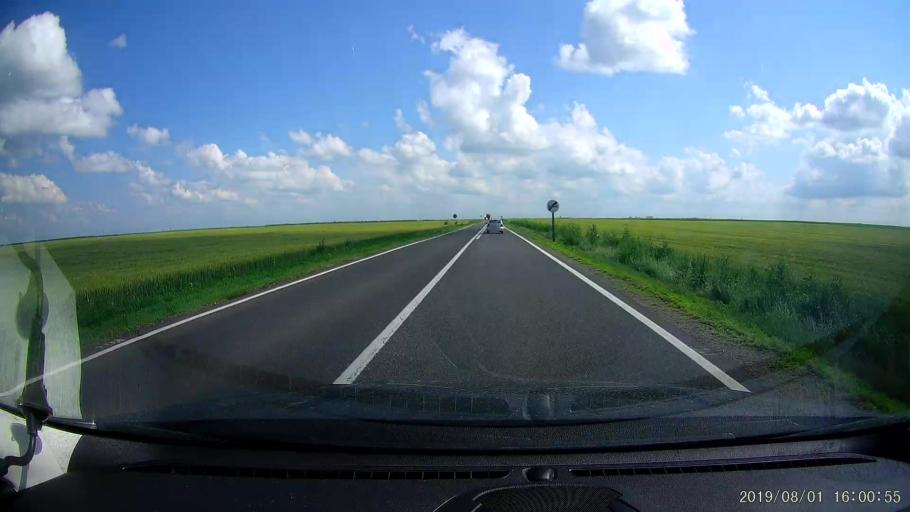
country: RO
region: Ialomita
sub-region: Comuna Ciulnita
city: Ciulnita
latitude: 44.5178
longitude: 27.3897
